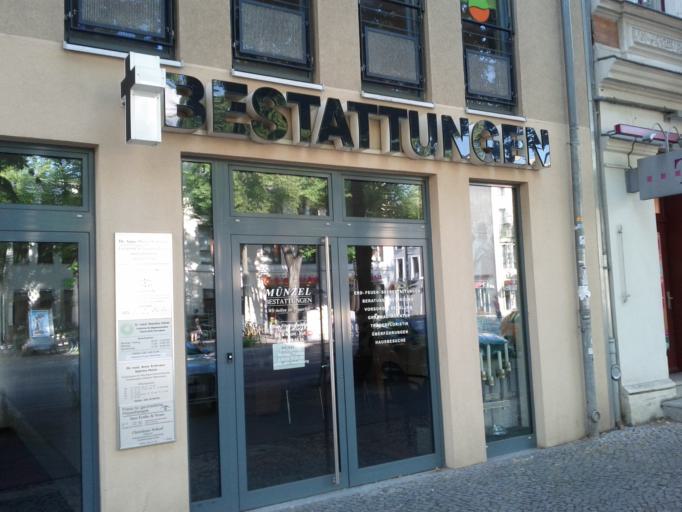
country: DE
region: Berlin
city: Friedrichshagen
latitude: 52.4513
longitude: 13.6246
